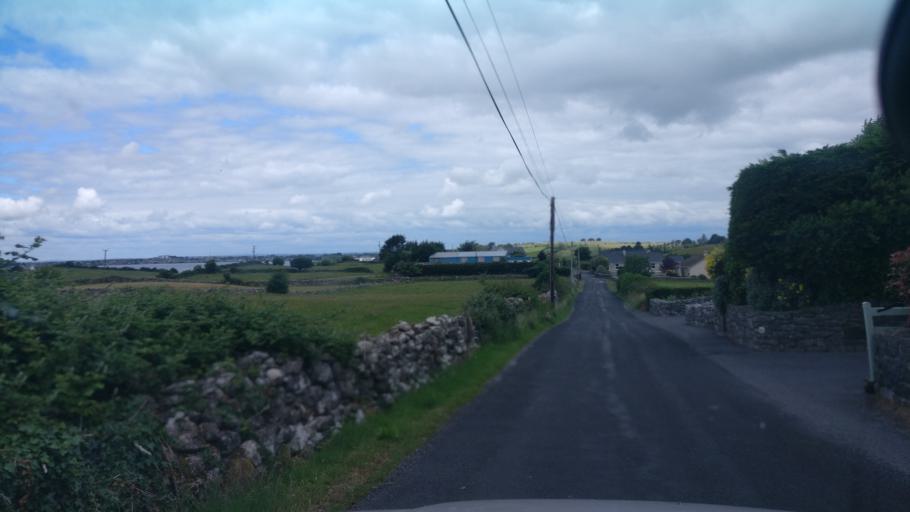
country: IE
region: Connaught
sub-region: County Galway
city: Loughrea
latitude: 53.1720
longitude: -8.5557
